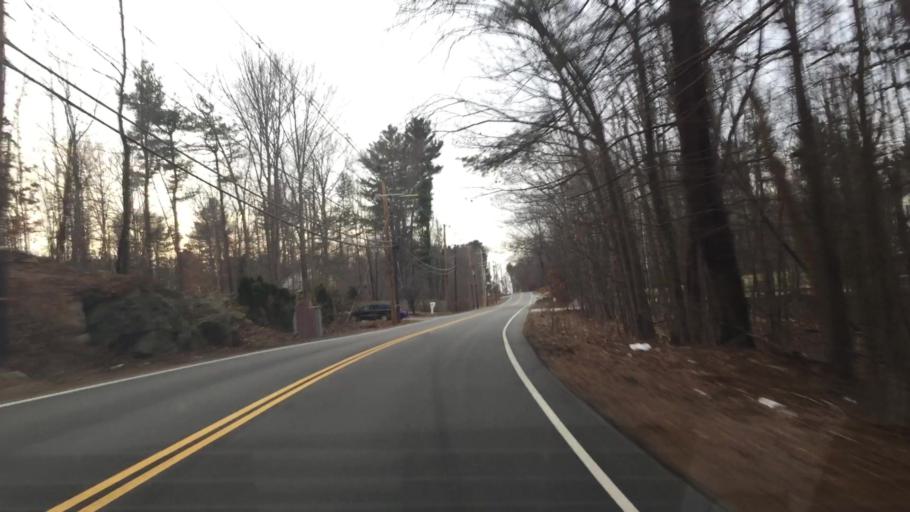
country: US
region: New Hampshire
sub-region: Hillsborough County
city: Pelham
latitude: 42.7477
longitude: -71.2751
